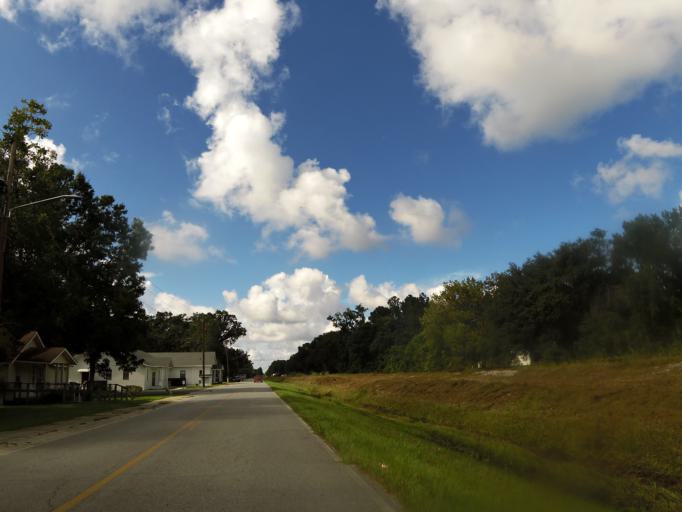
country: US
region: Georgia
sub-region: Camden County
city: Kingsland
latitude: 30.8034
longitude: -81.6921
